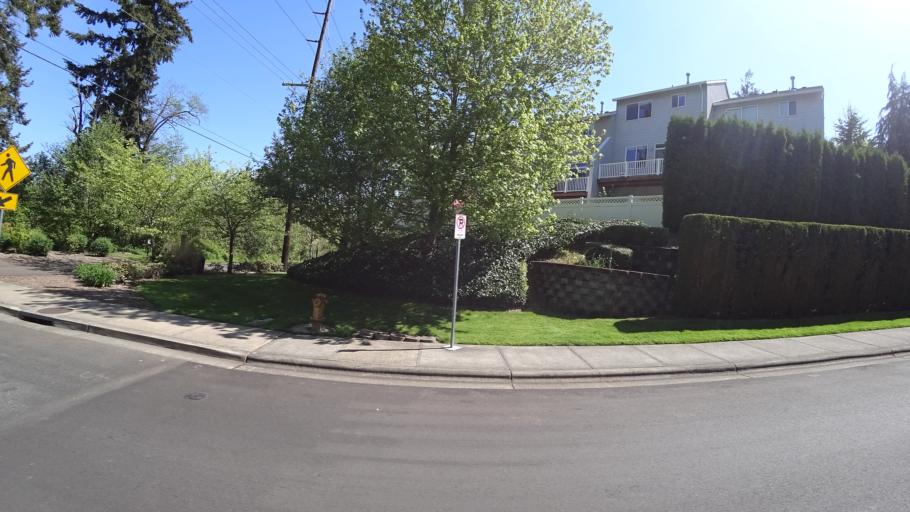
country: US
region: Oregon
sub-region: Washington County
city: King City
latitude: 45.4276
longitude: -122.8310
